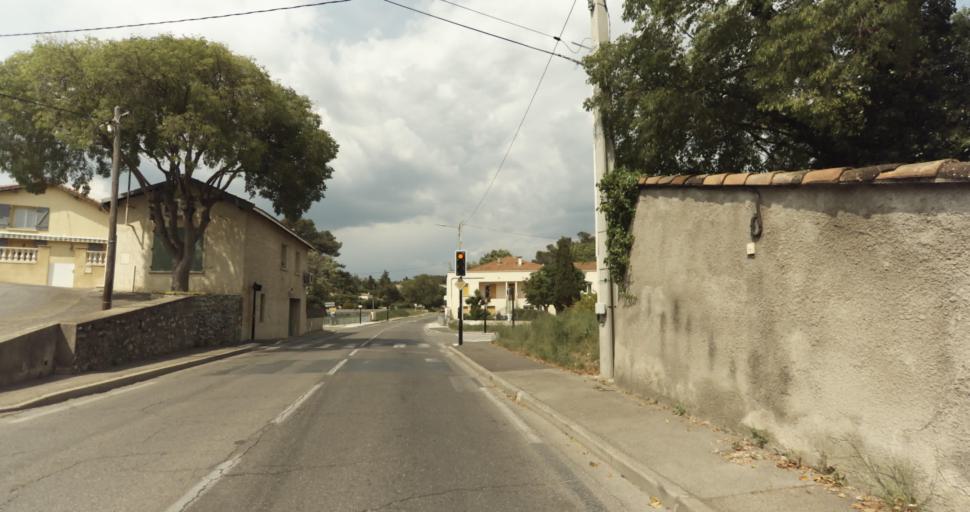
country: FR
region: Languedoc-Roussillon
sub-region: Departement du Gard
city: Nimes
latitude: 43.8453
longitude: 4.3456
